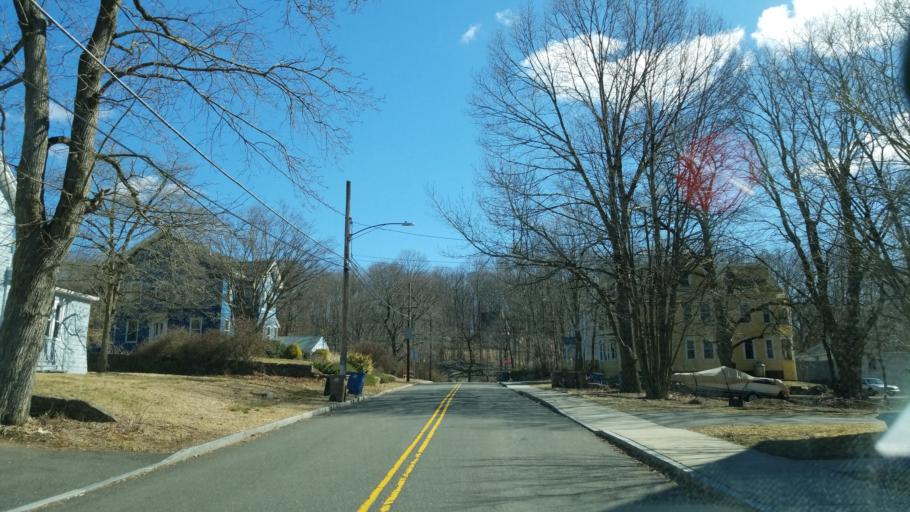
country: US
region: Connecticut
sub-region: Tolland County
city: Rockville
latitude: 41.8710
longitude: -72.4427
